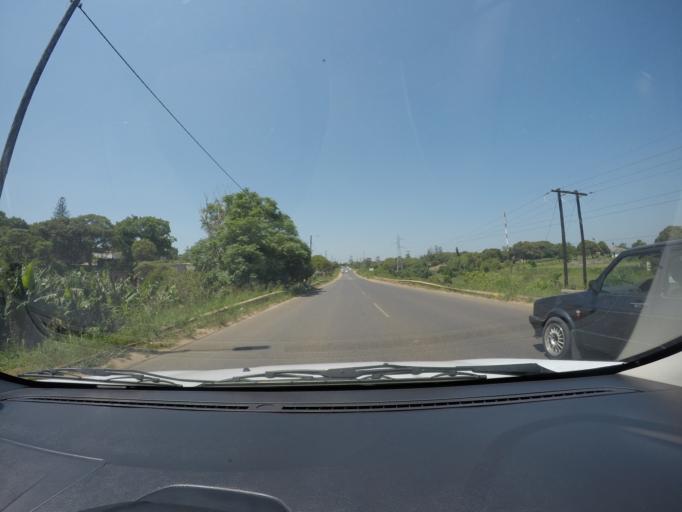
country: ZA
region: KwaZulu-Natal
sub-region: uThungulu District Municipality
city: eSikhawini
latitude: -28.8496
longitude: 31.9275
